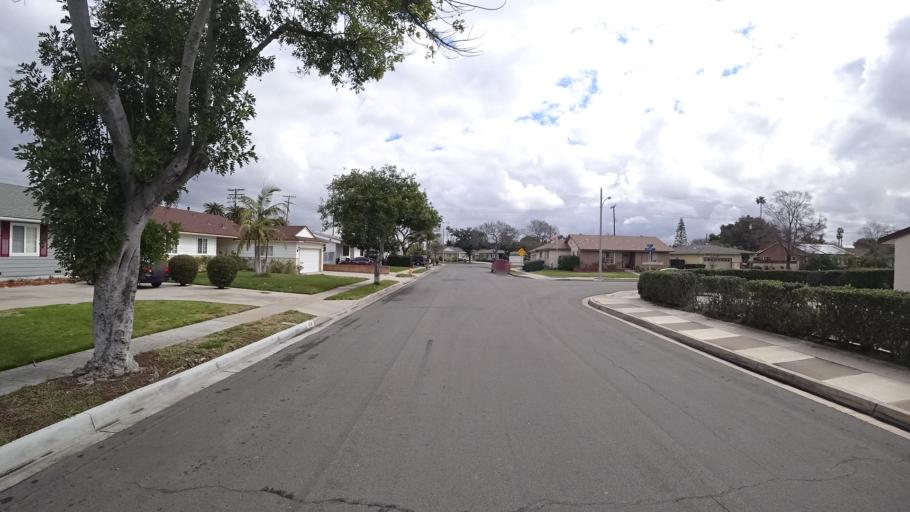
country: US
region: California
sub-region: Orange County
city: Anaheim
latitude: 33.8230
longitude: -117.9431
